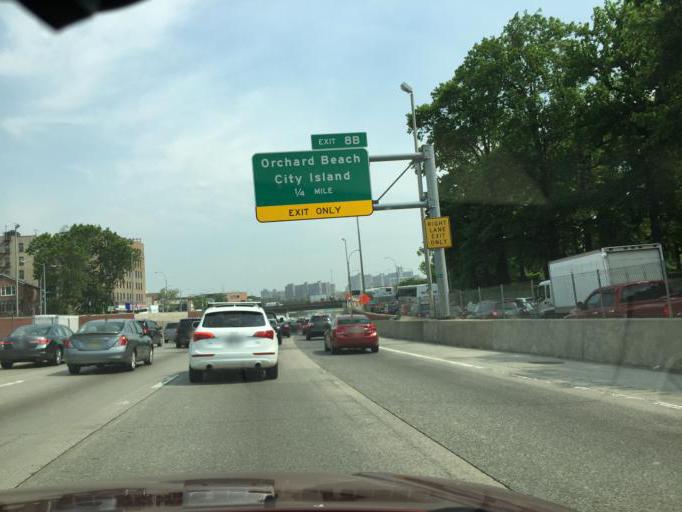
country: US
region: New York
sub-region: Bronx
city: Eastchester
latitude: 40.8501
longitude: -73.8272
